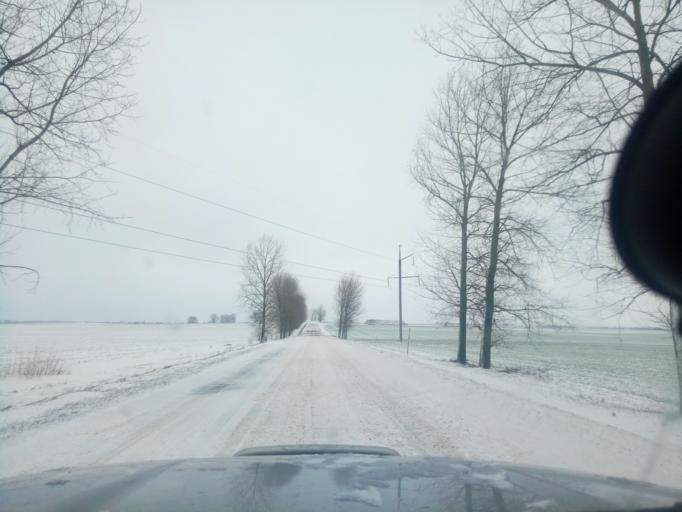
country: BY
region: Minsk
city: Tsimkavichy
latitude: 53.0544
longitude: 26.9394
